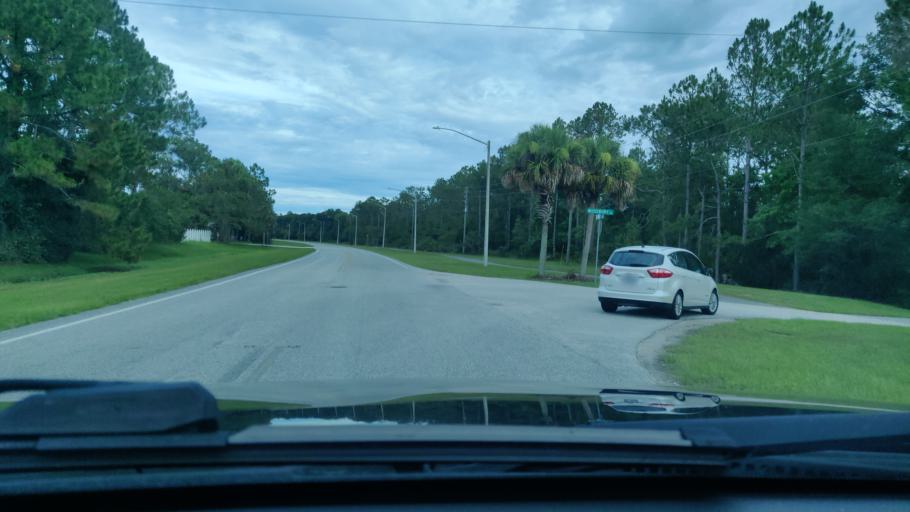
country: US
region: Florida
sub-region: Flagler County
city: Bunnell
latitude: 29.5311
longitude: -81.2519
